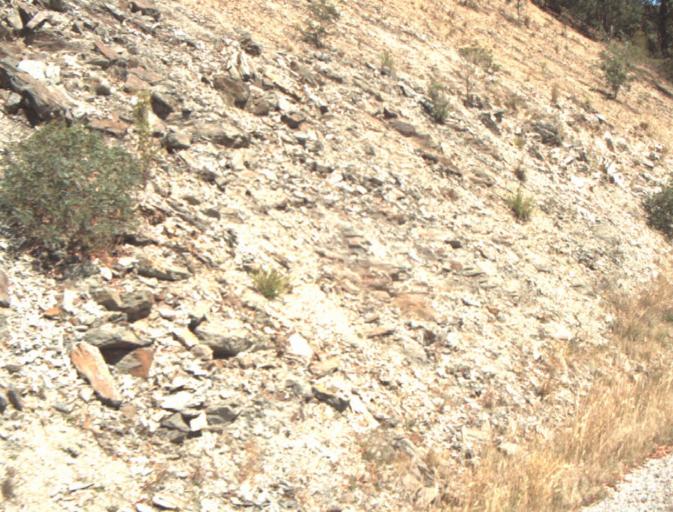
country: AU
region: Tasmania
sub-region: Dorset
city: Scottsdale
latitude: -41.3099
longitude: 147.3777
